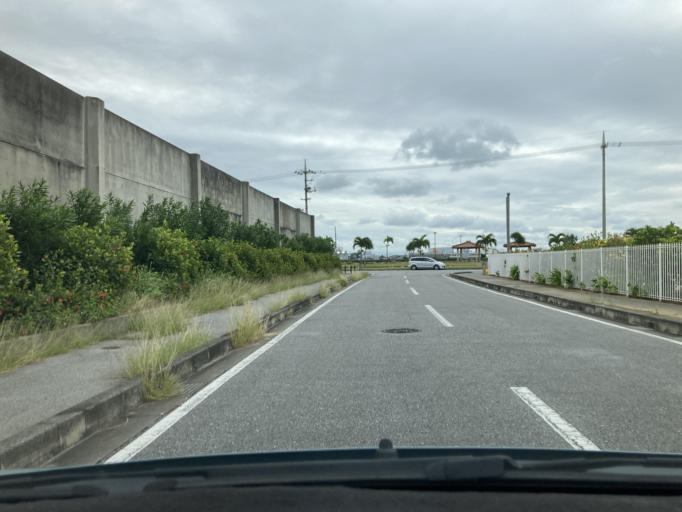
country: JP
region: Okinawa
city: Itoman
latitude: 26.1532
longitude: 127.6548
